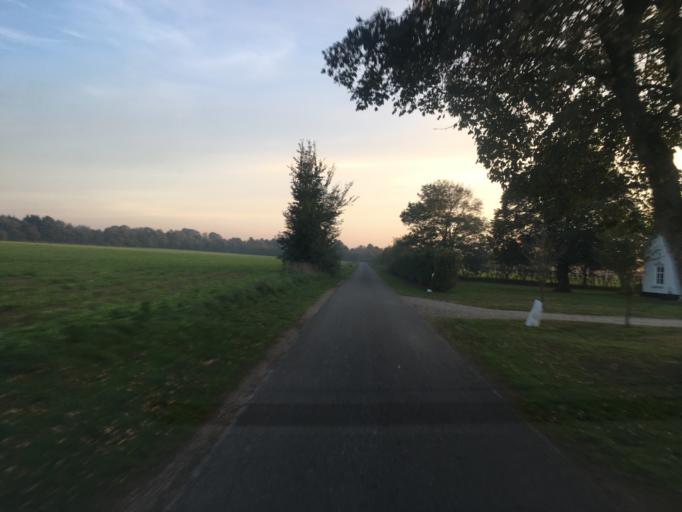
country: DK
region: South Denmark
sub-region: Aabenraa Kommune
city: Tinglev
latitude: 55.0153
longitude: 9.1236
